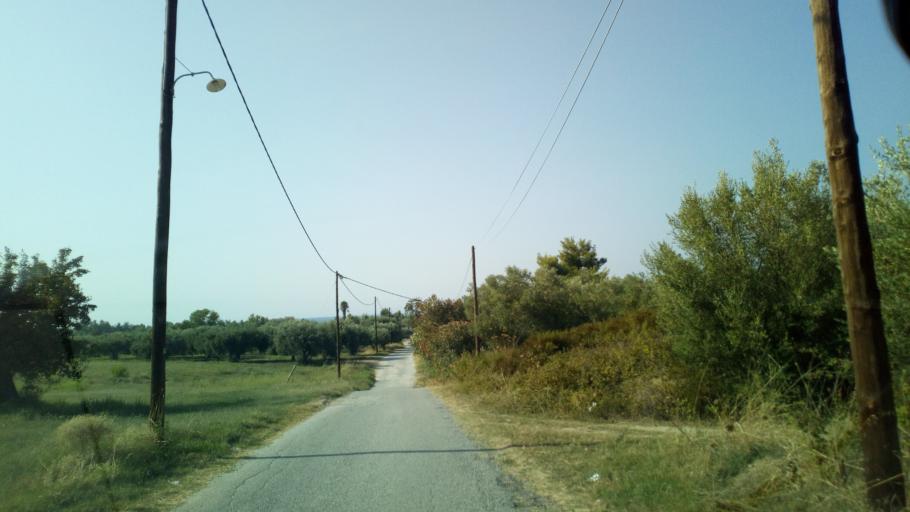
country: GR
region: Central Macedonia
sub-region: Nomos Chalkidikis
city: Pefkochori
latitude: 39.9745
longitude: 23.6526
